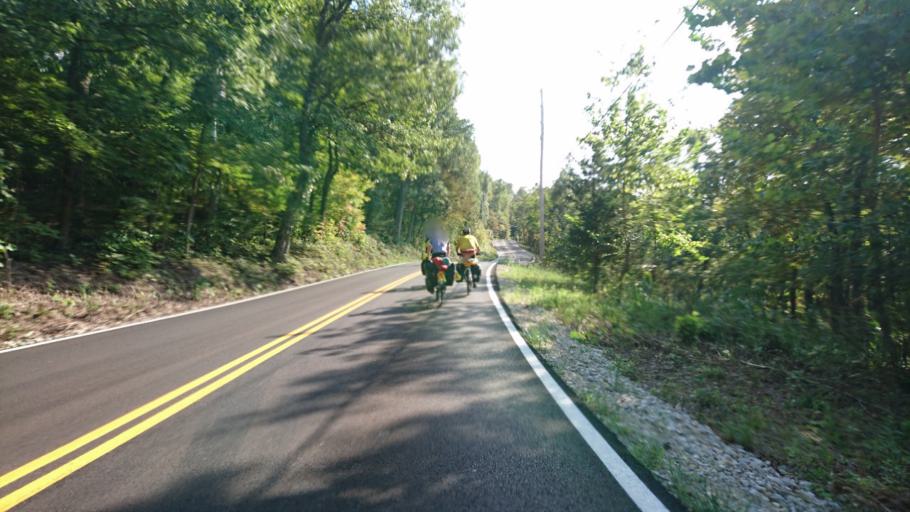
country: US
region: Missouri
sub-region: Saint Louis County
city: Eureka
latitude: 38.5322
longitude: -90.6404
